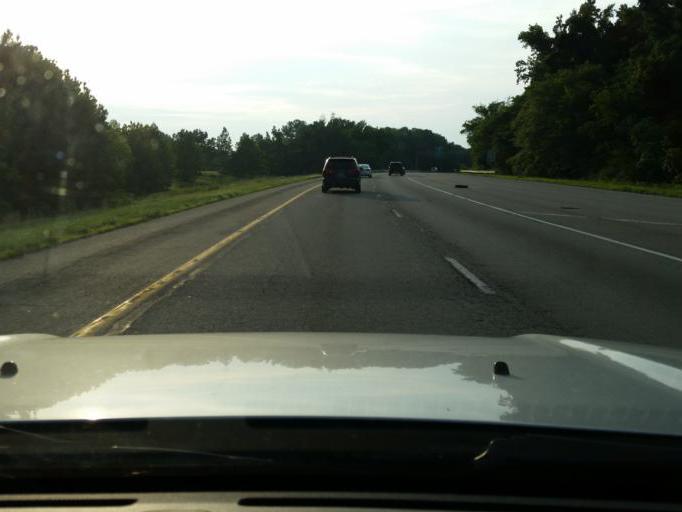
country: US
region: Virginia
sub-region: Henrico County
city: Chamberlayne
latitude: 37.6557
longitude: -77.4421
